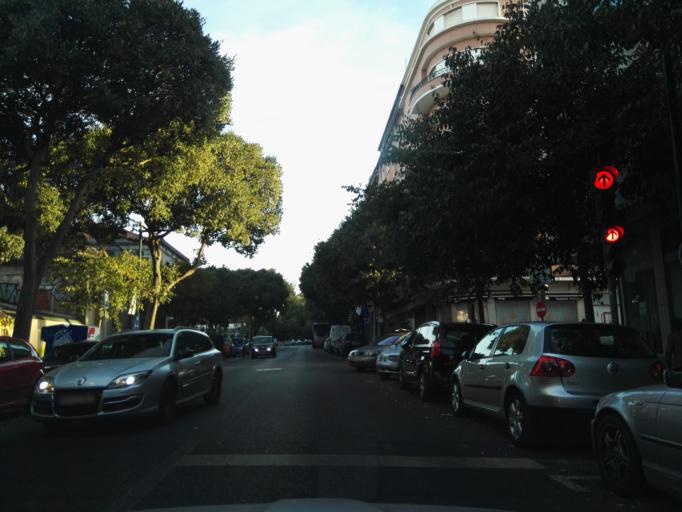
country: PT
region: Lisbon
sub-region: Lisbon
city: Lisbon
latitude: 38.7302
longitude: -9.1406
